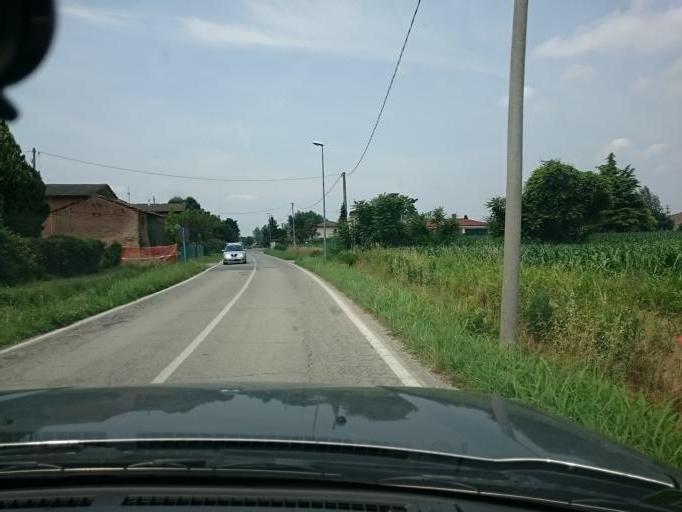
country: IT
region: Veneto
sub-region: Provincia di Padova
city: Sant'Angelo di Piove di Sacco
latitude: 45.3199
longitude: 11.9865
